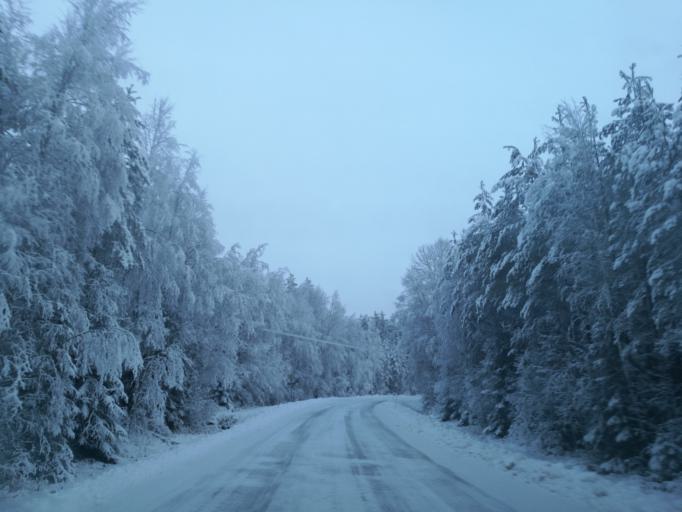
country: NO
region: Hedmark
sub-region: Grue
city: Kirkenaer
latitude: 60.4187
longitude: 12.4503
